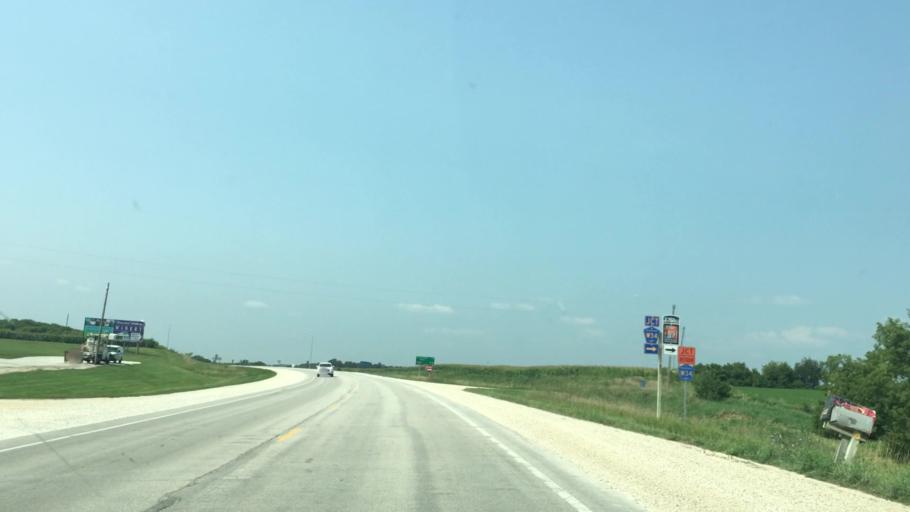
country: US
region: Iowa
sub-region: Winneshiek County
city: Decorah
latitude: 43.3649
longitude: -91.8047
